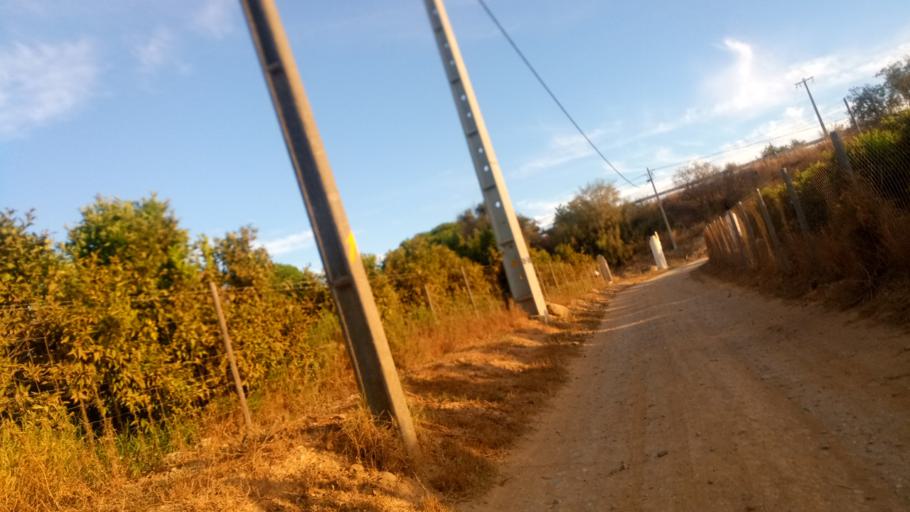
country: PT
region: Faro
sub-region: Tavira
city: Tavira
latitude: 37.1526
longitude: -7.5869
